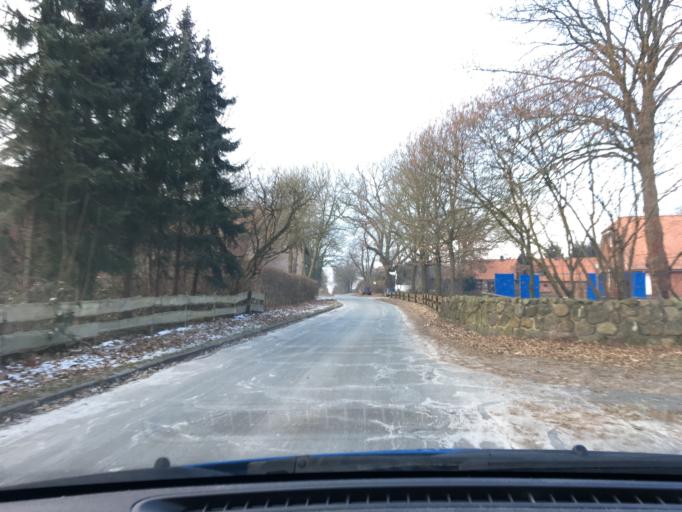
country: DE
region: Lower Saxony
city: Bienenbuttel
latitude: 53.1534
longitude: 10.4781
